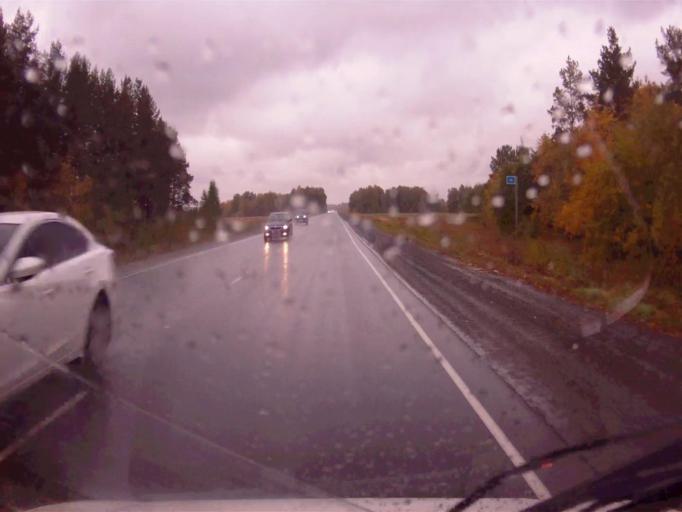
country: RU
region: Chelyabinsk
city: Roshchino
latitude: 55.3844
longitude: 61.1346
